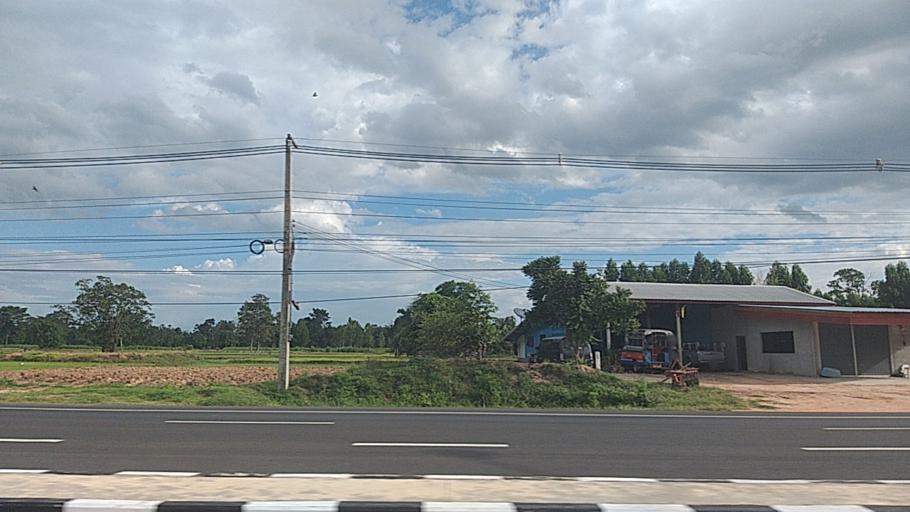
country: TH
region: Surin
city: Prasat
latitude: 14.5896
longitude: 103.4653
